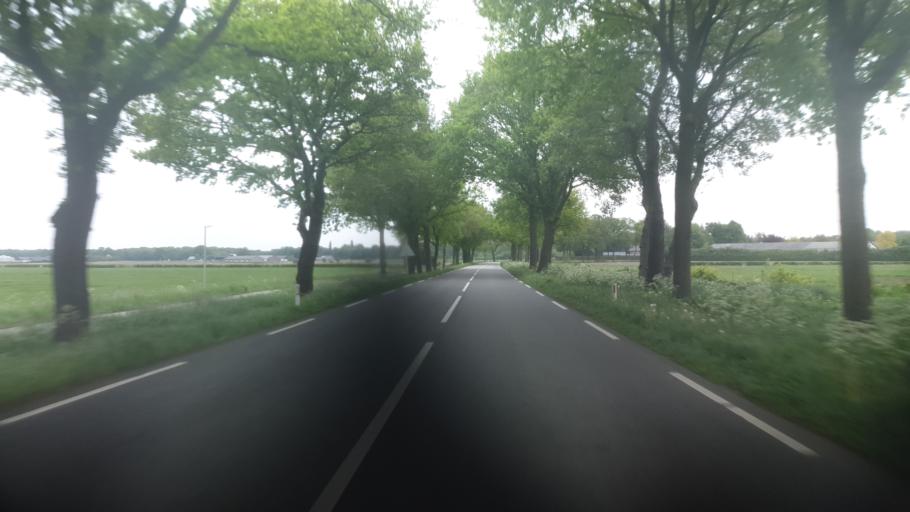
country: NL
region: North Brabant
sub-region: Gemeente Grave
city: Grave
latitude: 51.7734
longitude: 5.7898
